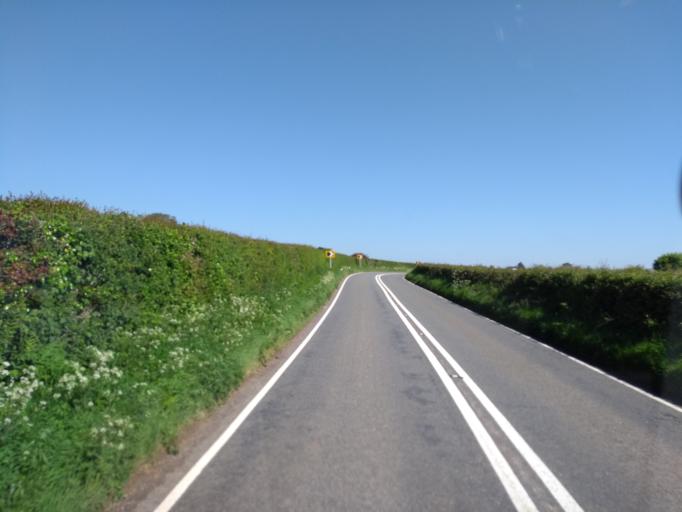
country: GB
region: England
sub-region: Somerset
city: Chard
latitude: 50.8334
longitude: -2.9627
